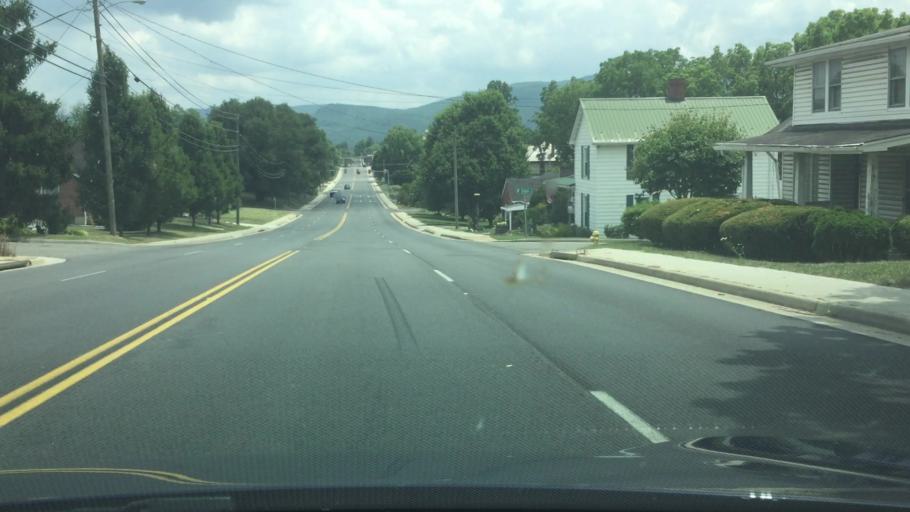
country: US
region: Virginia
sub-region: Wythe County
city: Wytheville
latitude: 36.9530
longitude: -81.0904
